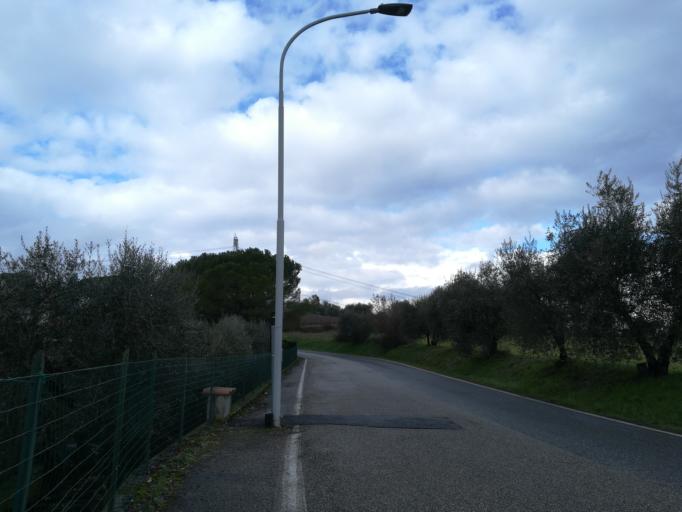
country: IT
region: Tuscany
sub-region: Provincia di Prato
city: Comeana
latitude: 43.7963
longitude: 11.0454
